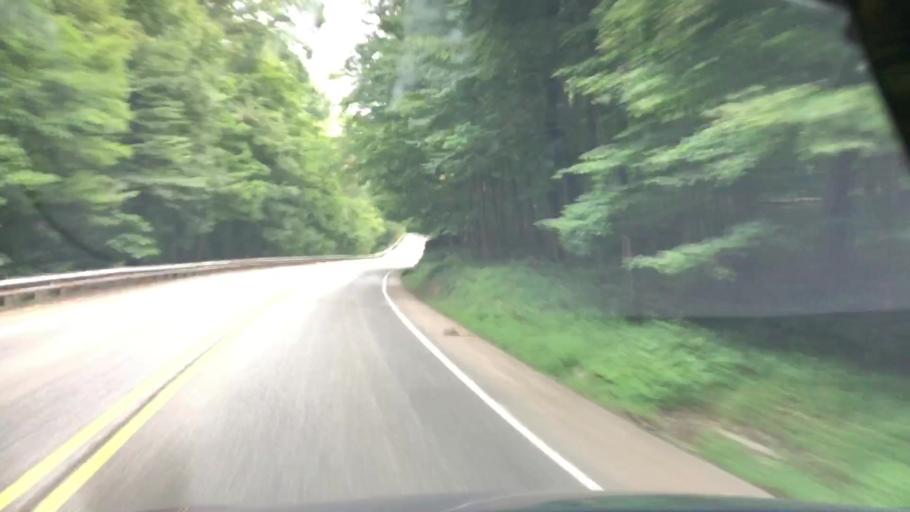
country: US
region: Pennsylvania
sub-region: Venango County
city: Hasson Heights
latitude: 41.5188
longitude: -79.7071
